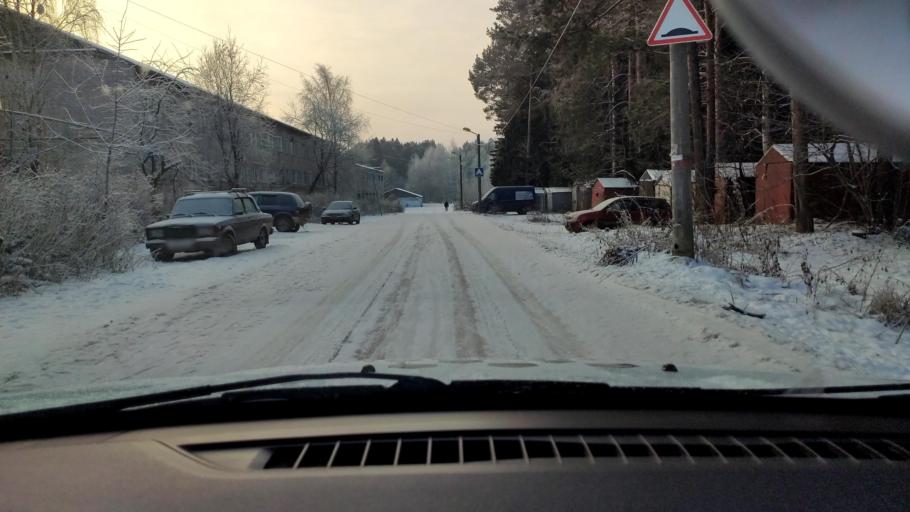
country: RU
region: Perm
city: Kondratovo
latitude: 58.0455
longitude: 56.1382
